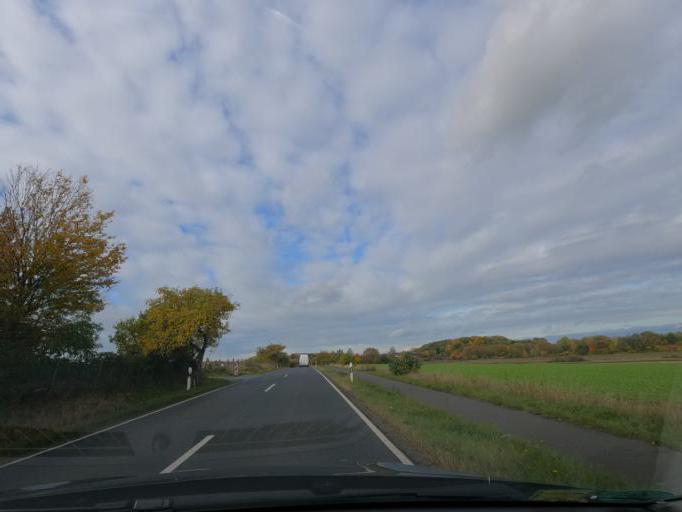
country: DE
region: Lower Saxony
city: Leiferde
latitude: 52.1817
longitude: 10.4995
